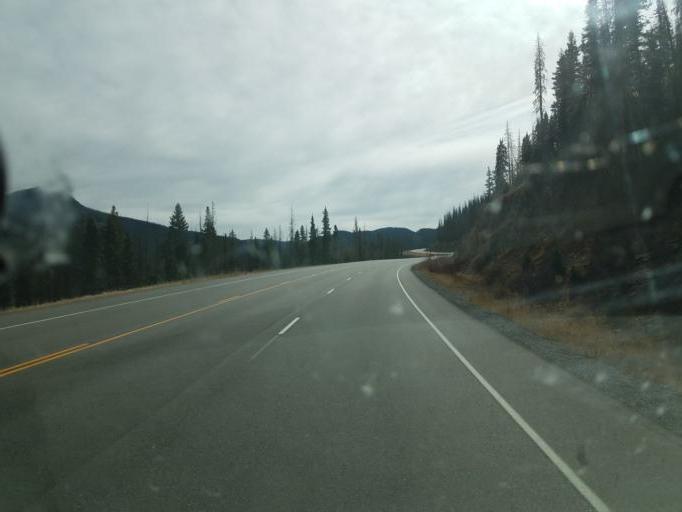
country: US
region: Colorado
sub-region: Archuleta County
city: Pagosa Springs
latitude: 37.5027
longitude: -106.7720
